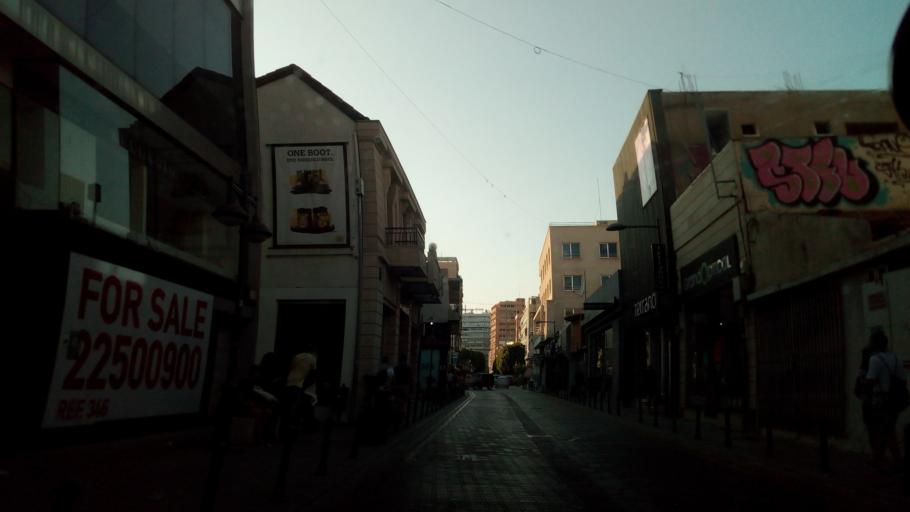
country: CY
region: Limassol
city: Limassol
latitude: 34.6779
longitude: 33.0448
